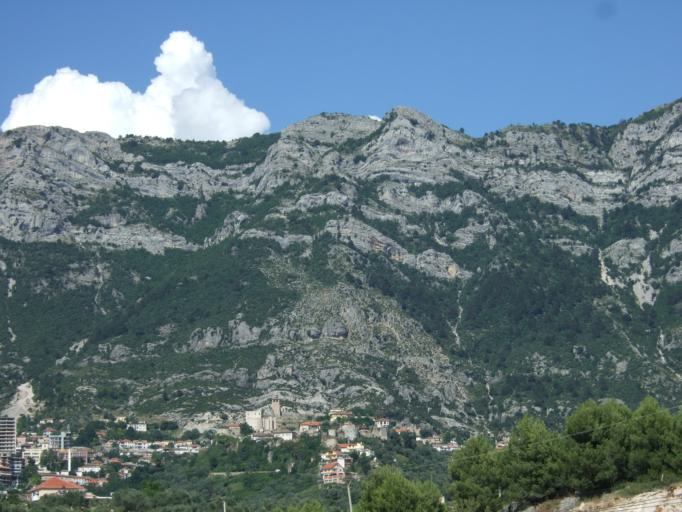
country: AL
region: Durres
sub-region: Rrethi i Krujes
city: Kruje
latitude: 41.4984
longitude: 19.7769
